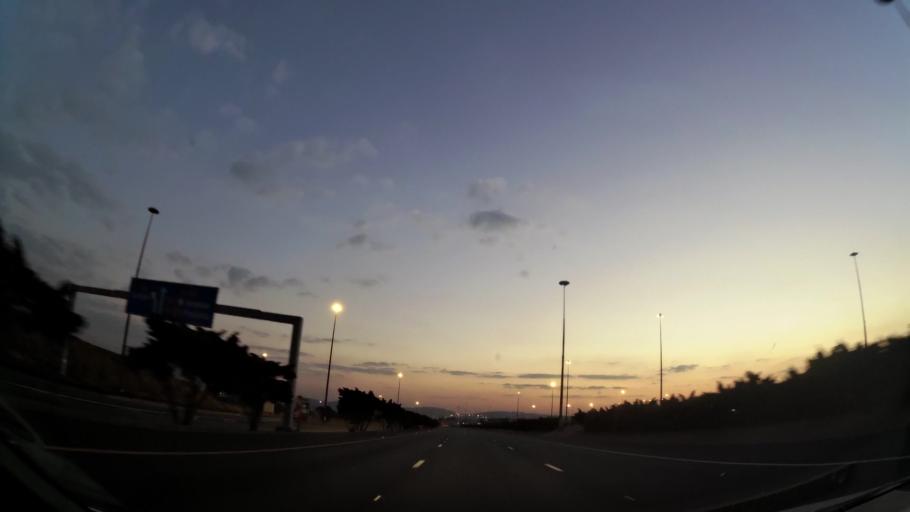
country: ZA
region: Gauteng
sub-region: Ekurhuleni Metropolitan Municipality
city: Germiston
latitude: -26.2493
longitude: 28.1529
